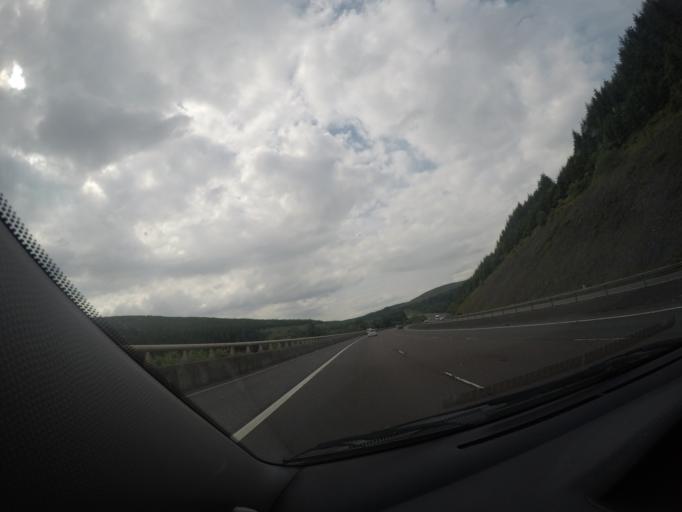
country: GB
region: Scotland
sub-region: Dumfries and Galloway
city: Moffat
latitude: 55.4013
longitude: -3.5529
